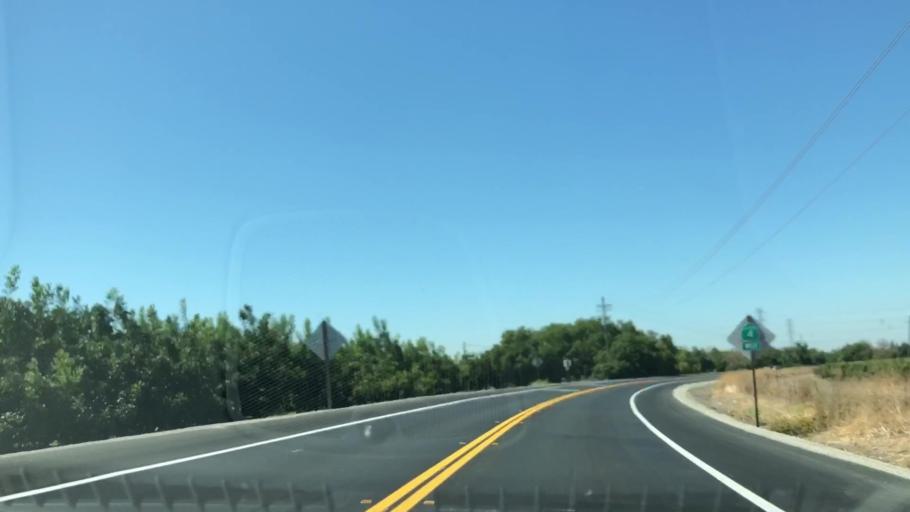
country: US
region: California
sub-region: San Joaquin County
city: Garden Acres
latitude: 37.9421
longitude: -121.1509
